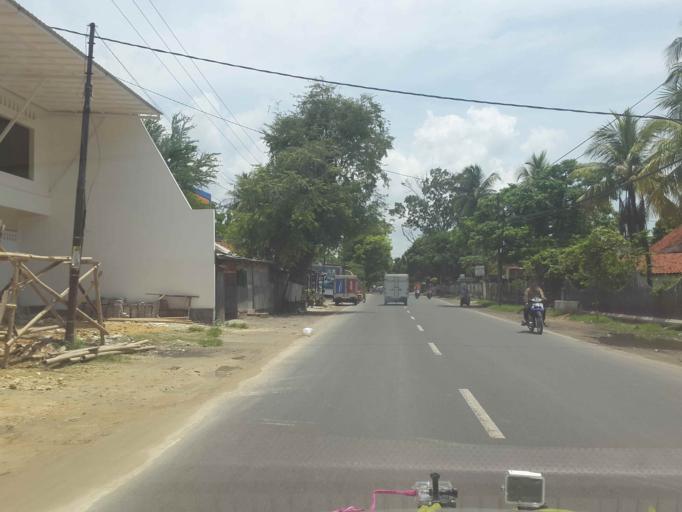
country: ID
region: East Java
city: Pragaan
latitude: -7.1103
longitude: 113.6658
